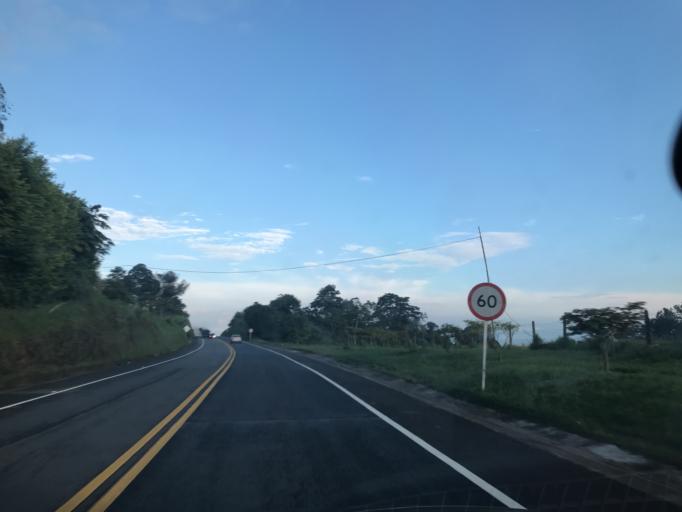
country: CO
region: Risaralda
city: Pereira
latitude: 4.7478
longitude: -75.6827
